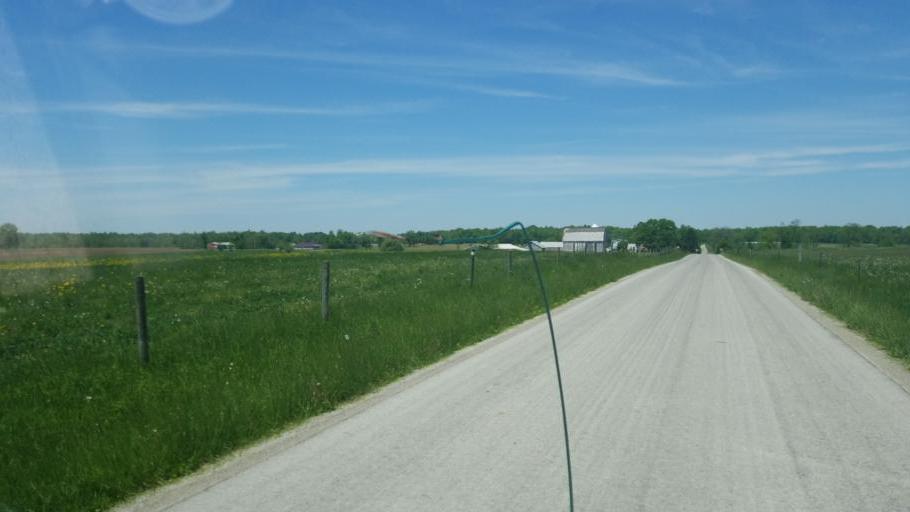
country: US
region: Ohio
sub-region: Huron County
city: Greenwich
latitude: 40.9709
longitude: -82.4318
